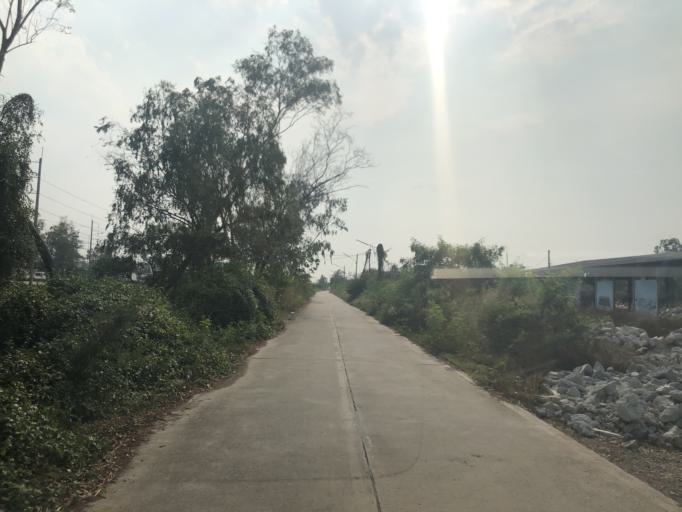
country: TH
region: Chachoengsao
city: Bang Pakong
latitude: 13.5059
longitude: 100.9769
